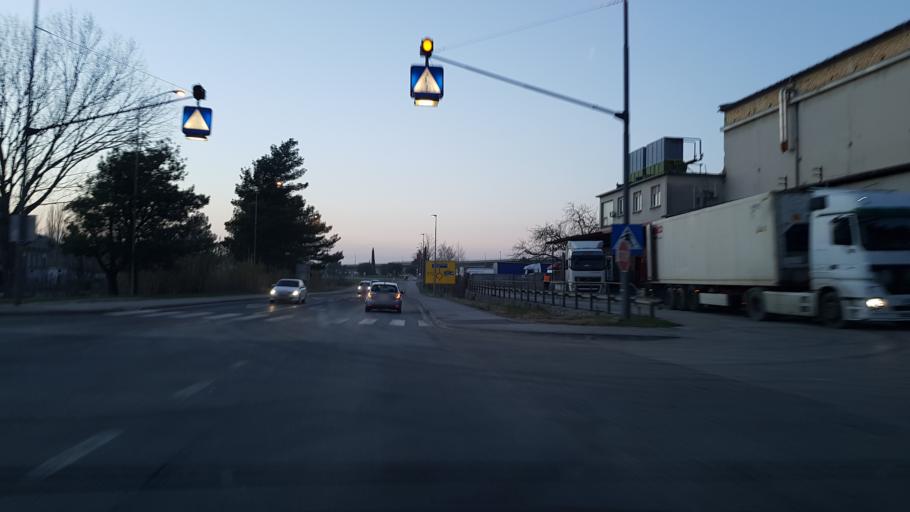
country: SI
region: Koper-Capodistria
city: Spodnje Skofije
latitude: 45.5568
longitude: 13.7889
